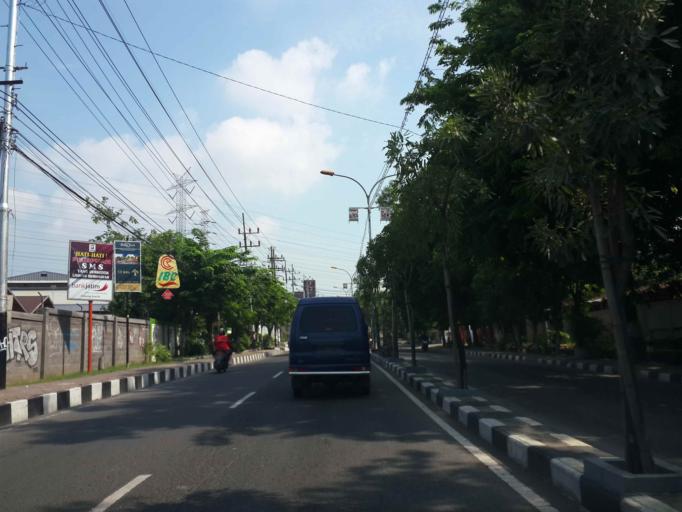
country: ID
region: East Java
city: Kebomas
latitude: -7.1874
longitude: 112.6474
